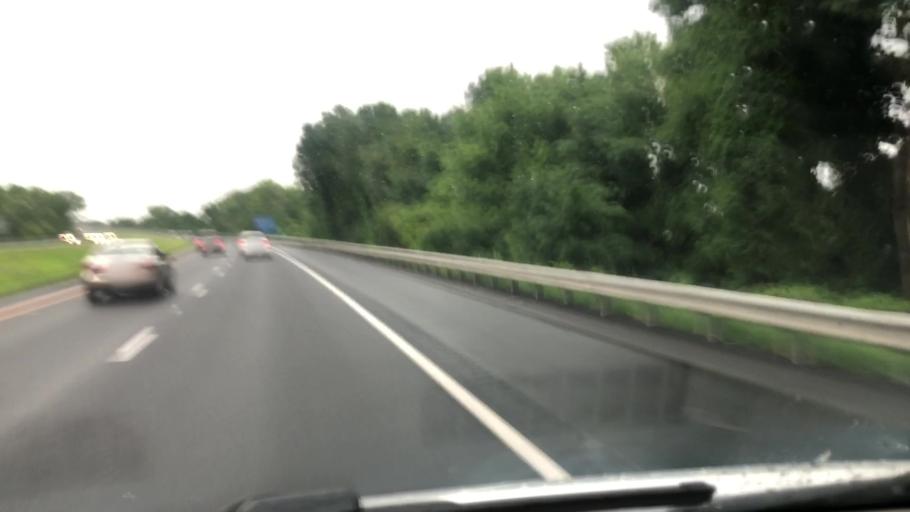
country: US
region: Massachusetts
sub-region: Hampshire County
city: Northampton
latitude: 42.3192
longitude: -72.6154
